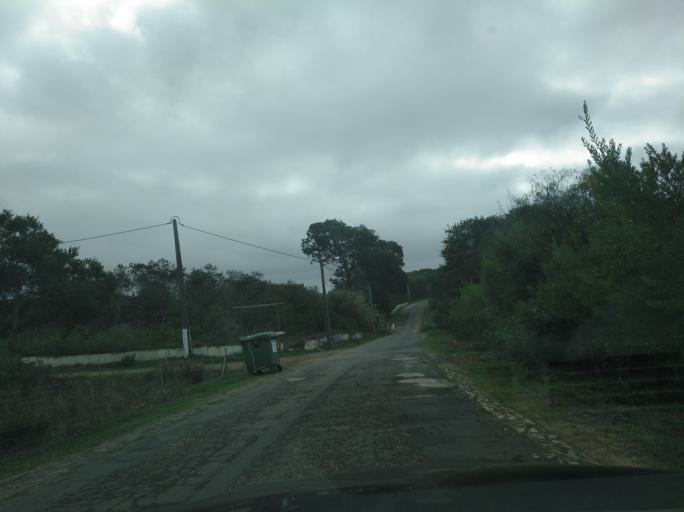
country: PT
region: Setubal
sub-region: Sines
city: Porto Covo
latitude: 37.8322
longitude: -8.7869
